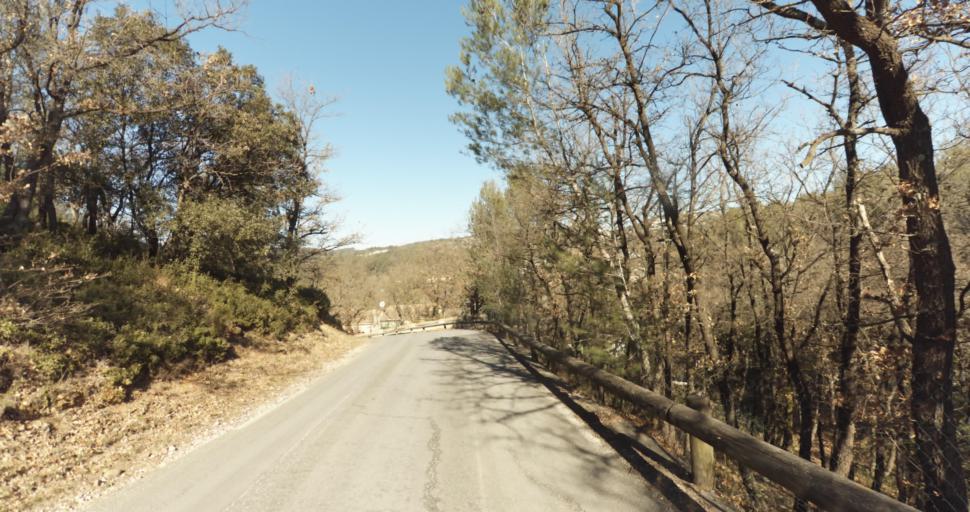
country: FR
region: Provence-Alpes-Cote d'Azur
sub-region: Departement des Bouches-du-Rhone
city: Peypin
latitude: 43.3903
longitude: 5.5854
